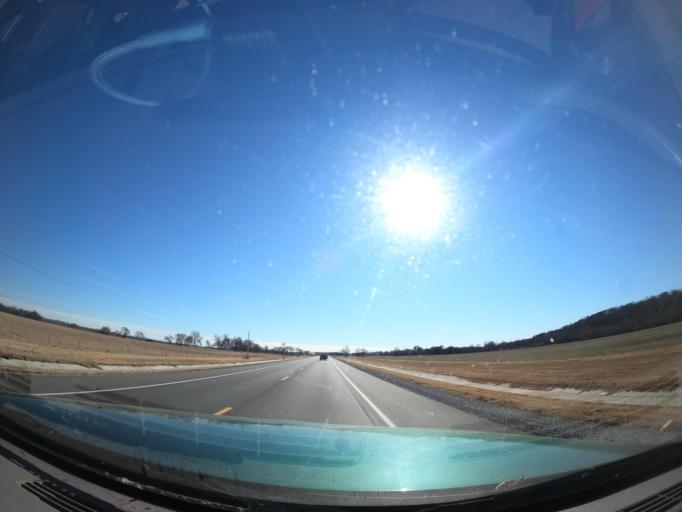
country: US
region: Oklahoma
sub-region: Wagoner County
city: Coweta
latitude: 35.8979
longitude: -95.6592
